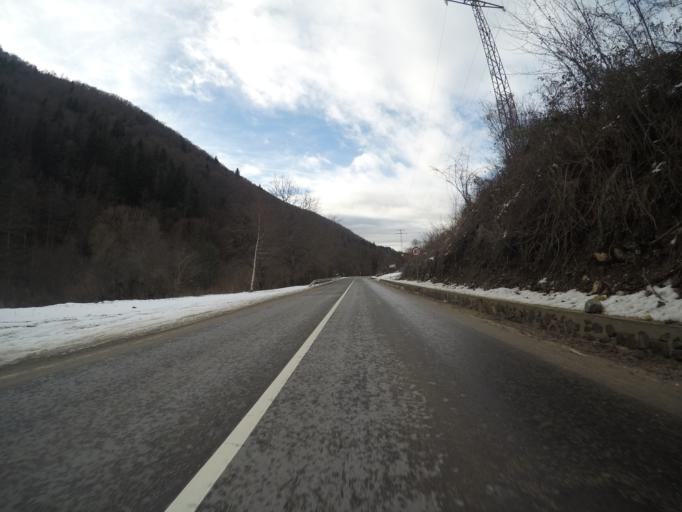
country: BG
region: Kyustendil
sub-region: Obshtina Rila
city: Rila
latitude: 42.1149
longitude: 23.3002
